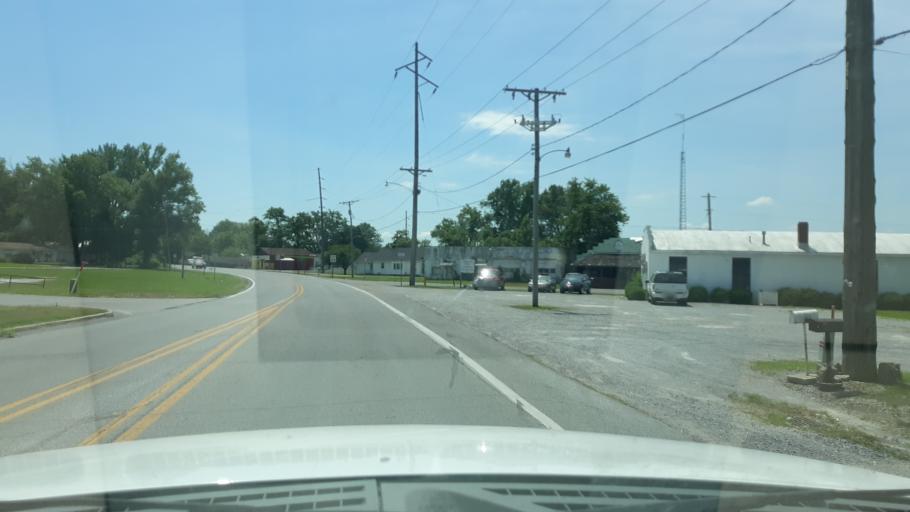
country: US
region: Illinois
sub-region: Saline County
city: Eldorado
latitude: 37.8063
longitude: -88.4395
